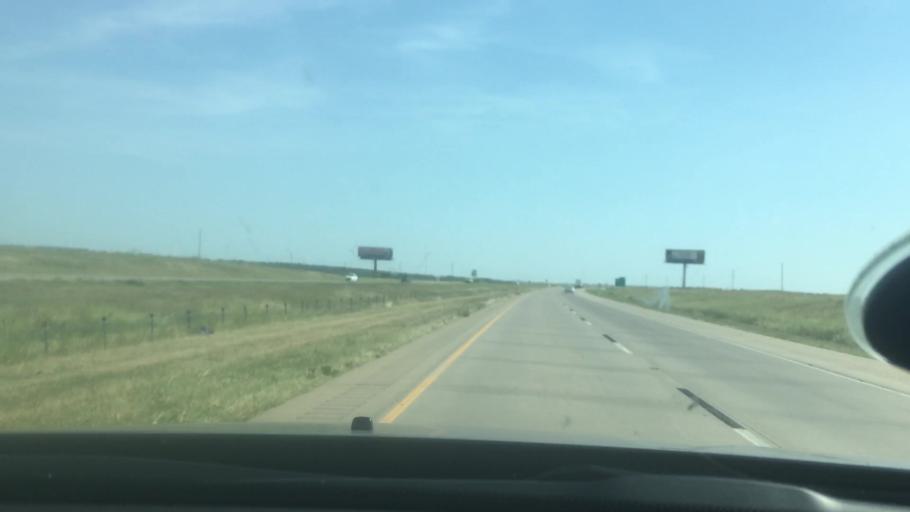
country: US
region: Oklahoma
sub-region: Carter County
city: Ardmore
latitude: 34.3251
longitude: -97.1549
